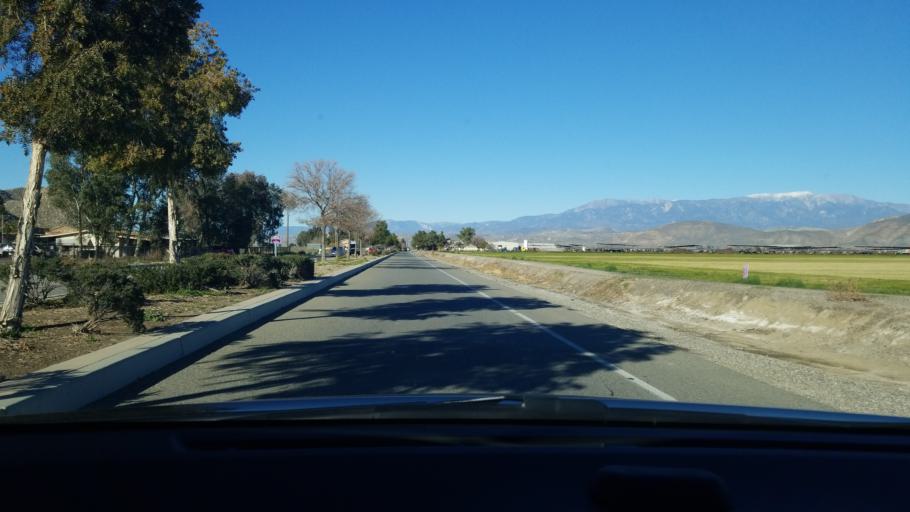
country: US
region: California
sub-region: Riverside County
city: Green Acres
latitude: 33.7914
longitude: -117.0336
